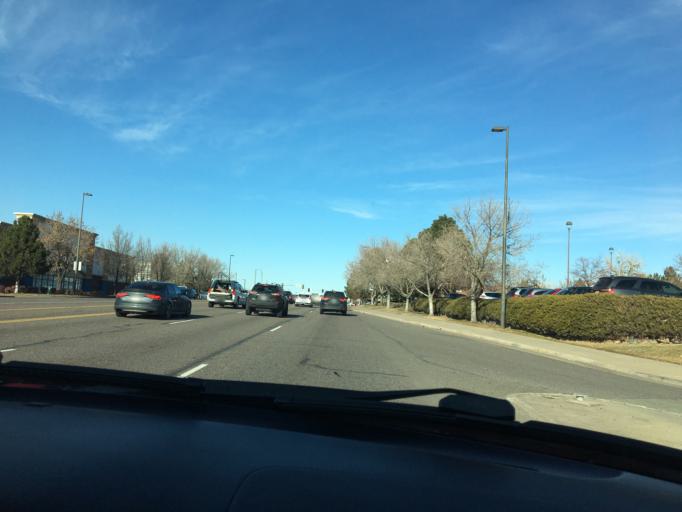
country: US
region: Colorado
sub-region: Adams County
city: Aurora
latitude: 39.6729
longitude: -104.8659
